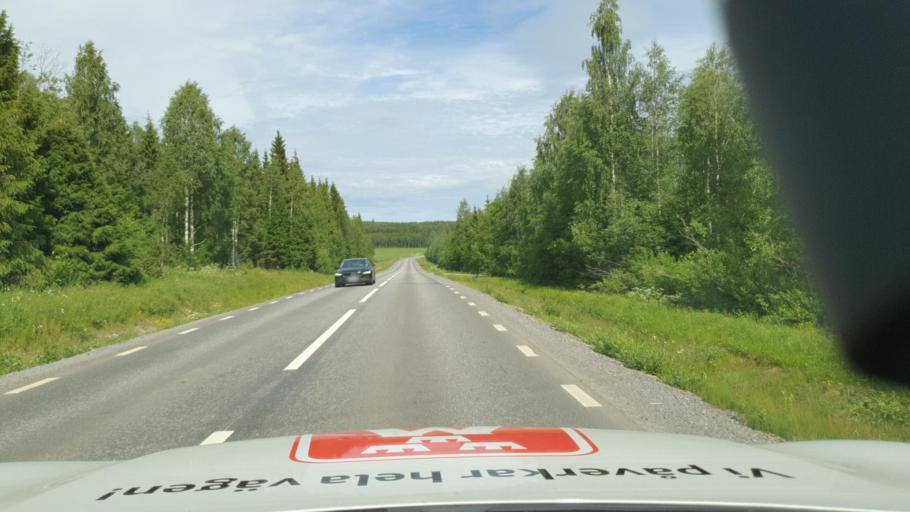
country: SE
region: Vaesterbotten
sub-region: Skelleftea Kommun
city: Burtraesk
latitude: 64.3774
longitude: 20.5099
